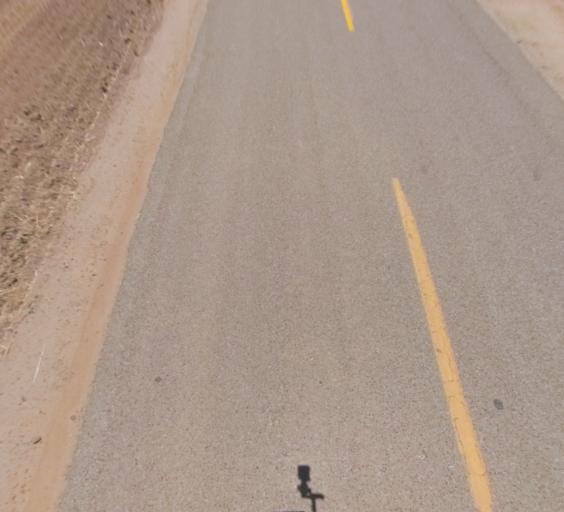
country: US
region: California
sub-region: Madera County
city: Bonadelle Ranchos-Madera Ranchos
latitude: 36.8742
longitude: -119.8208
